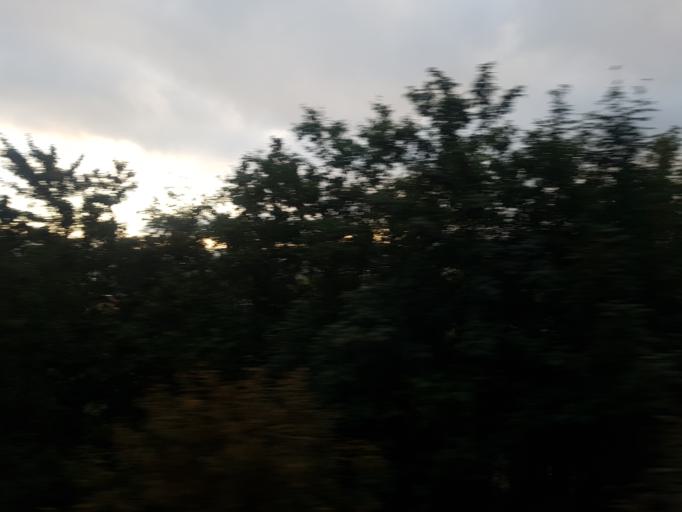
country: NO
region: Sor-Trondelag
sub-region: Trondheim
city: Trondheim
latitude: 63.4001
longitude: 10.4004
